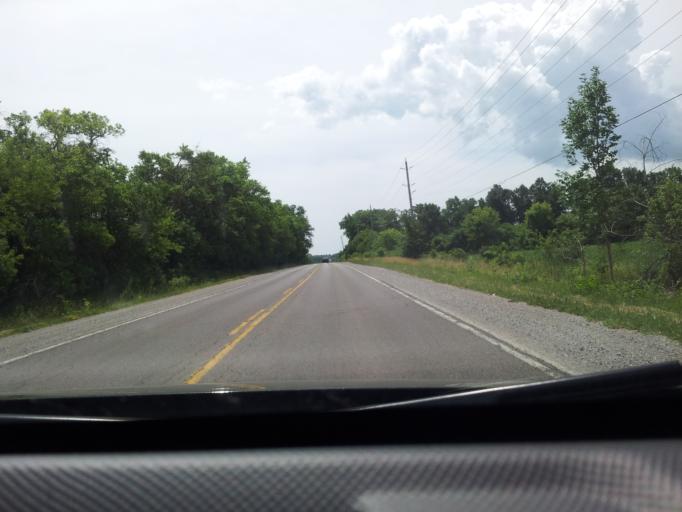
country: CA
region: Ontario
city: Norfolk County
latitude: 42.8152
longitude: -80.2501
